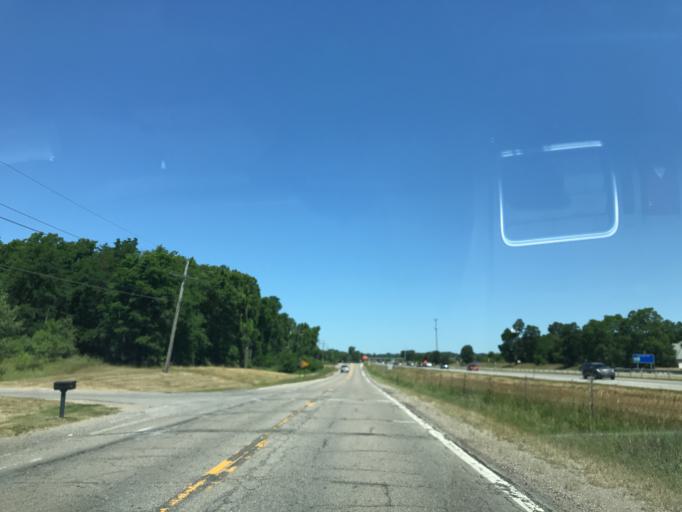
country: US
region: Michigan
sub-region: Livingston County
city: Brighton
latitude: 42.4970
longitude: -83.7581
